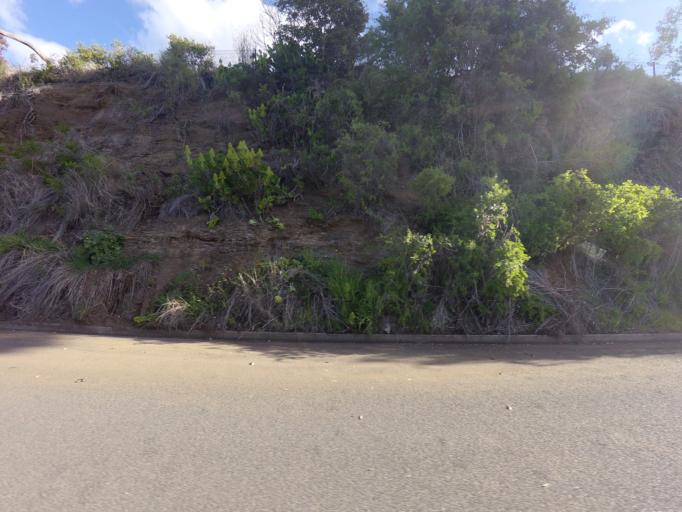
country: AU
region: Tasmania
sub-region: Glenorchy
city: Lutana
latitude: -42.8476
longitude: 147.3254
